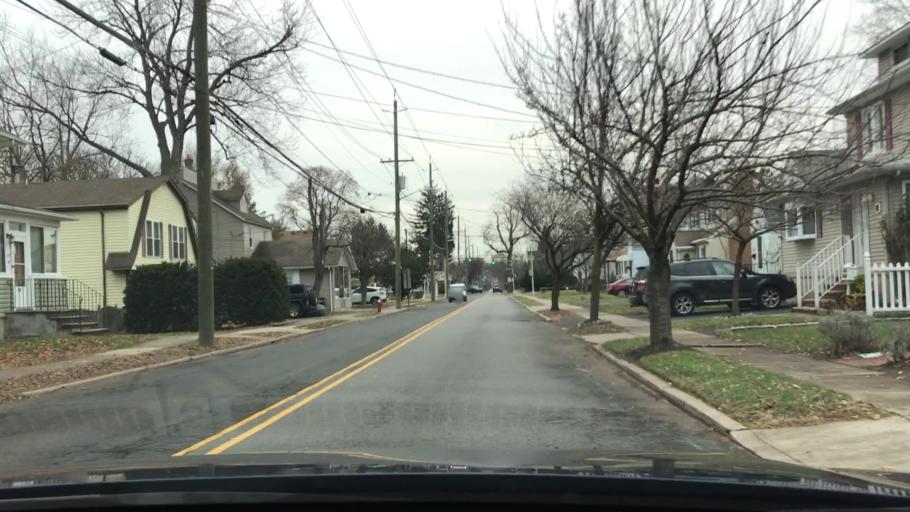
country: US
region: New Jersey
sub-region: Bergen County
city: New Milford
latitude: 40.9416
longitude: -74.0162
